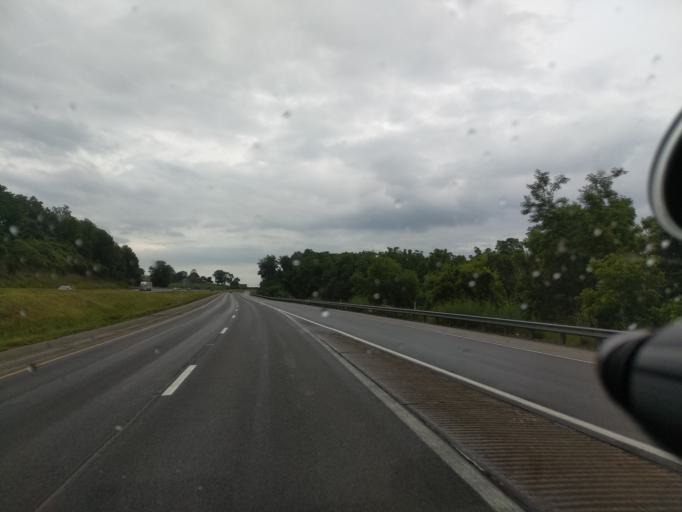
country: US
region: Pennsylvania
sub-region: Northumberland County
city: Milton
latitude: 41.0223
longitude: -76.7946
